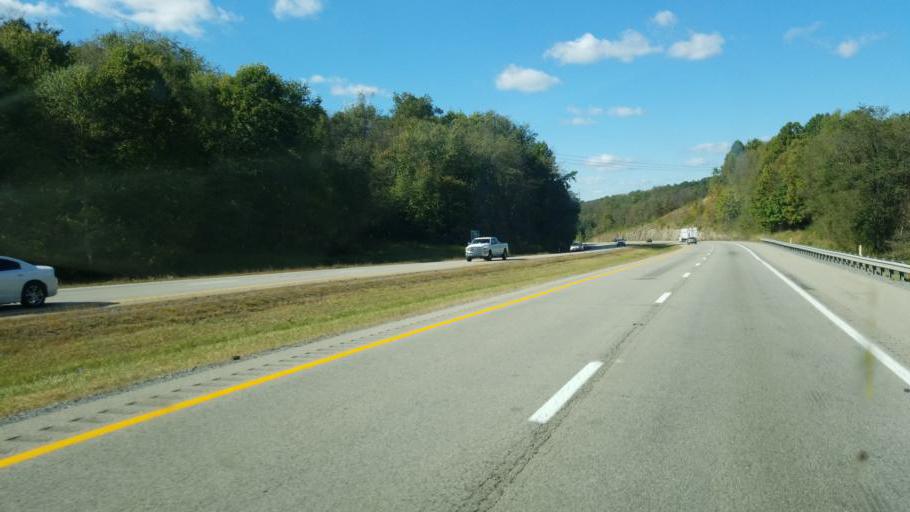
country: US
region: West Virginia
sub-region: Monongalia County
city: Star City
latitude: 39.7084
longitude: -80.0553
